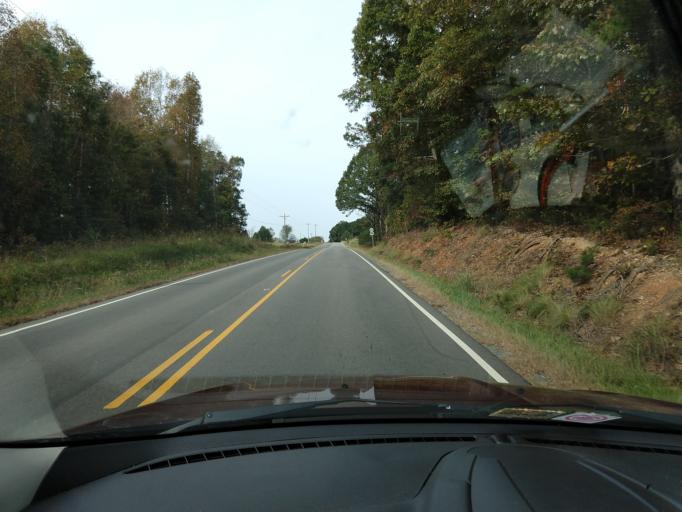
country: US
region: Virginia
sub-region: Franklin County
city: Union Hall
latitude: 36.9647
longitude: -79.5829
